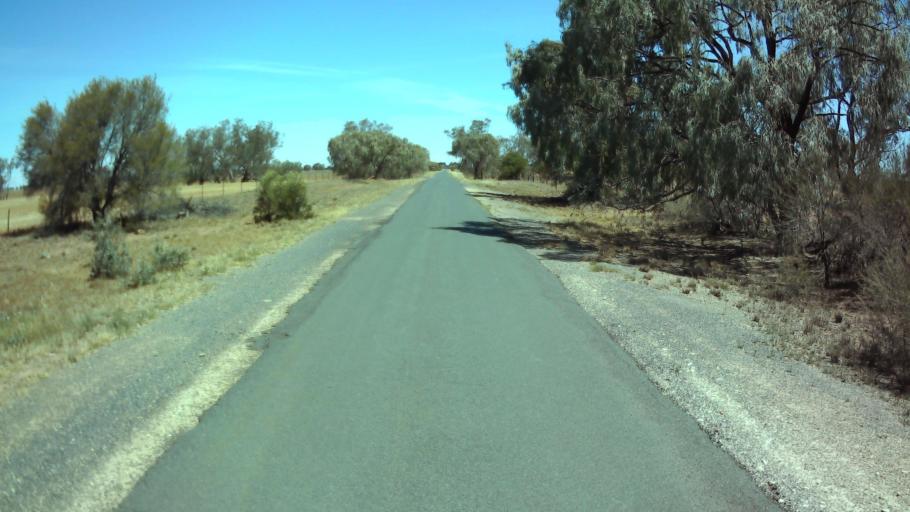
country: AU
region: New South Wales
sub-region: Weddin
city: Grenfell
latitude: -33.8477
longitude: 147.6961
